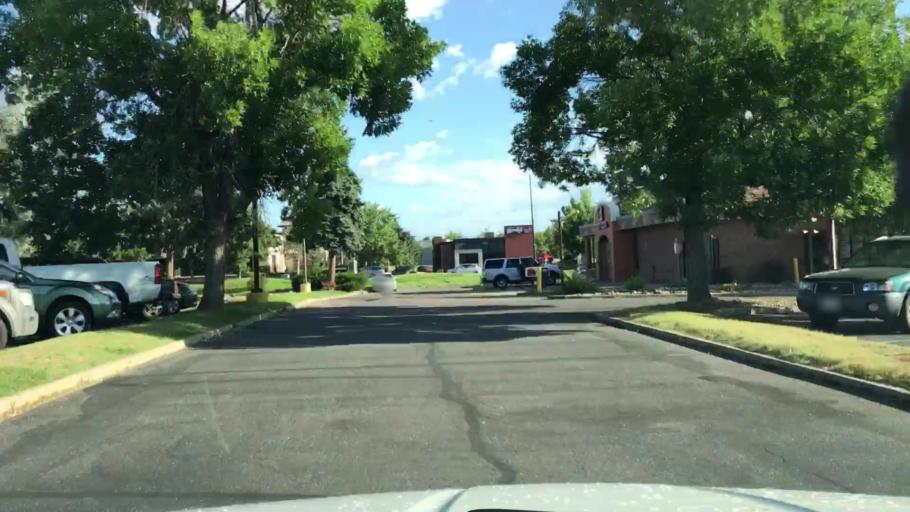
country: US
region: Colorado
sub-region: Boulder County
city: Lafayette
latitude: 39.9861
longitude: -105.0952
